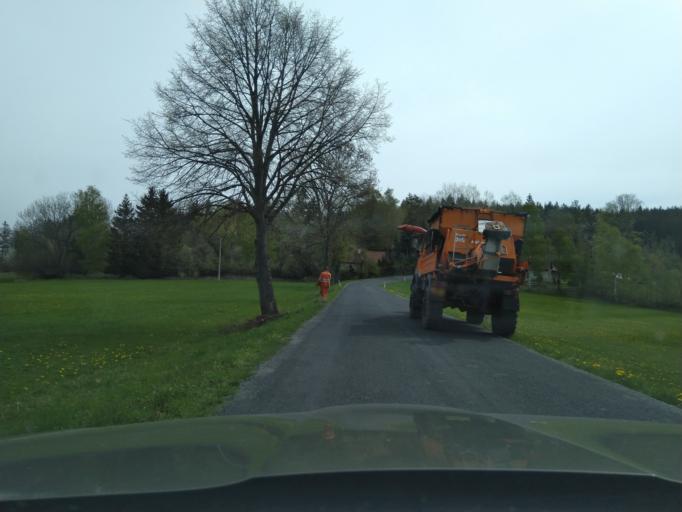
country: CZ
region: Jihocesky
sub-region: Okres Prachatice
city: Stachy
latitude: 49.1795
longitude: 13.6547
